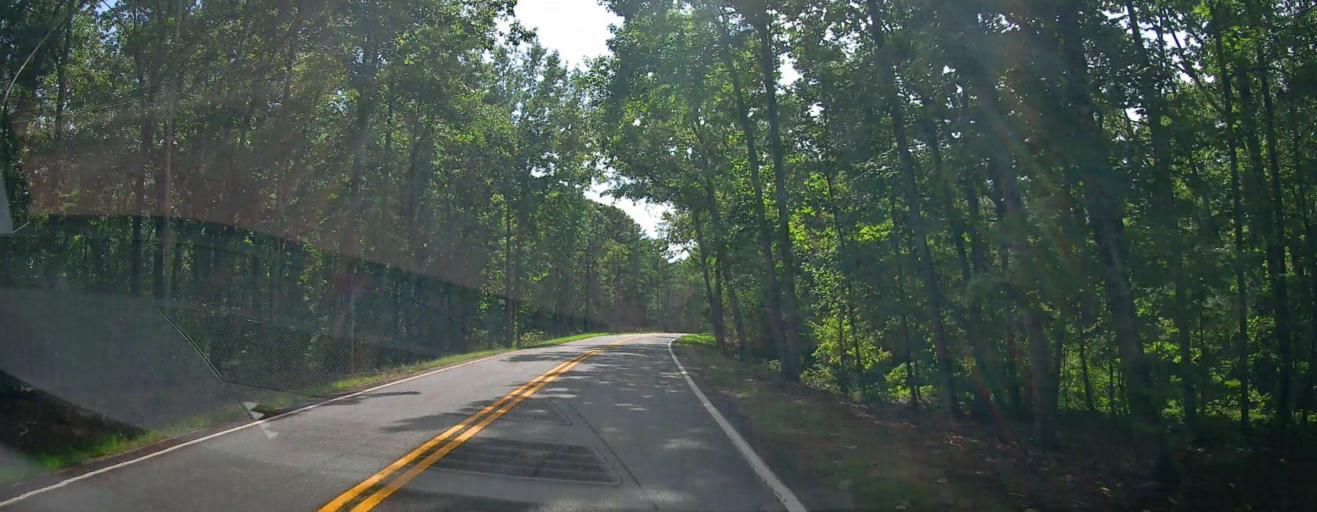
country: US
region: Georgia
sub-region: Talbot County
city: Sardis
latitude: 32.8572
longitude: -84.7379
